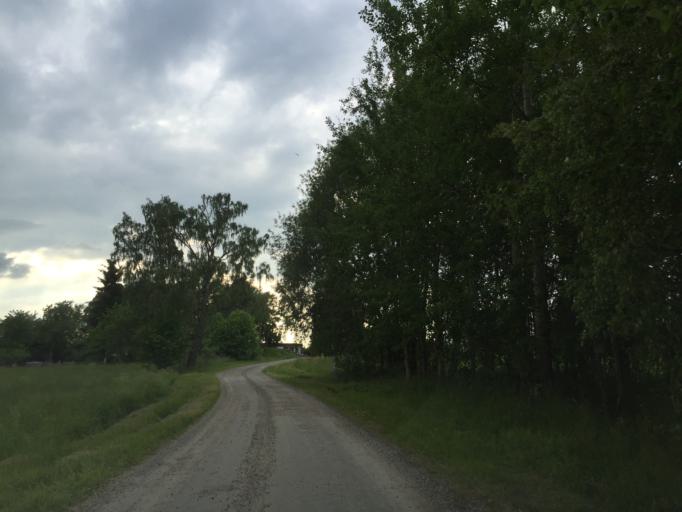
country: SE
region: OErebro
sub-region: Lindesbergs Kommun
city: Fellingsbro
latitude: 59.3260
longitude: 15.5328
